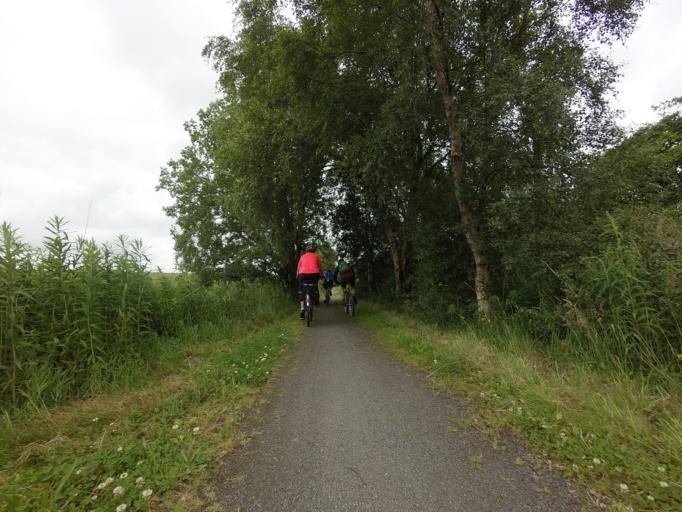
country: GB
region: Scotland
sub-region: Aberdeenshire
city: Ellon
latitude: 57.4783
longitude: -2.1304
